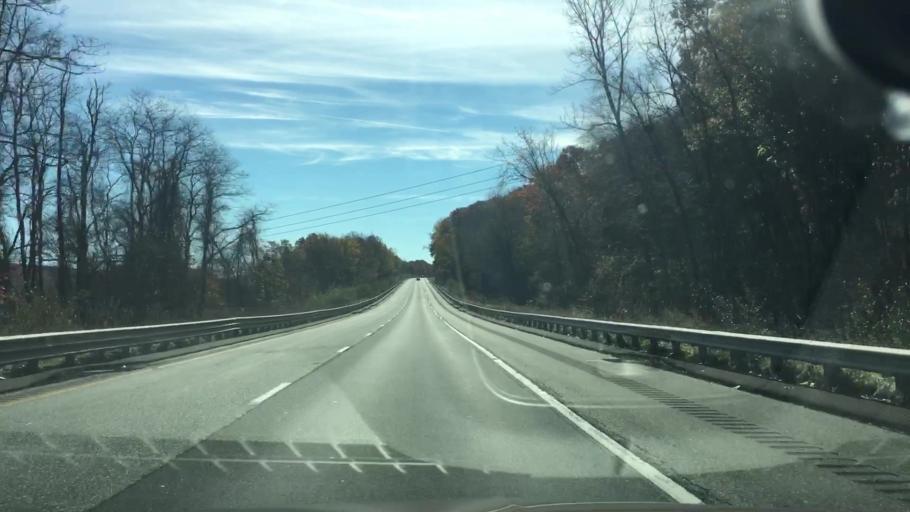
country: US
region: Massachusetts
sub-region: Franklin County
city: Greenfield
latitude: 42.5673
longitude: -72.6208
